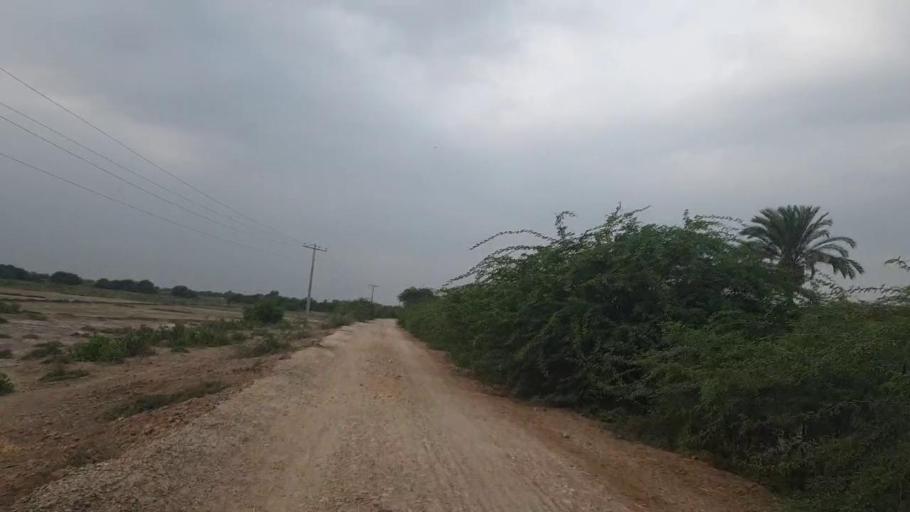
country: PK
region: Sindh
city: Badin
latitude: 24.6147
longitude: 68.6840
